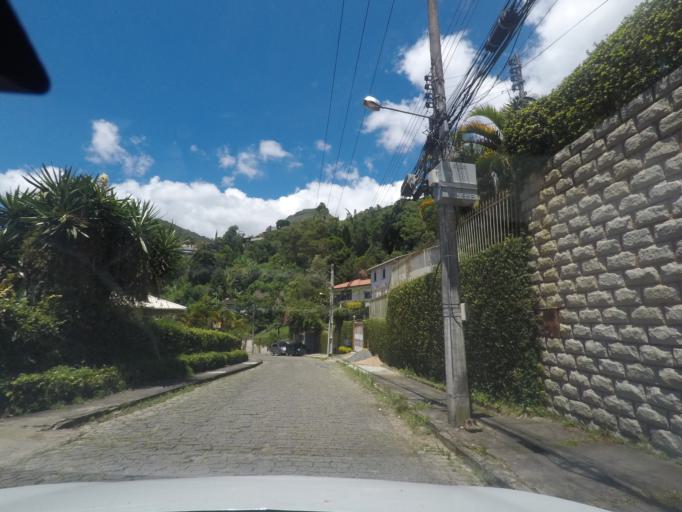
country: BR
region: Rio de Janeiro
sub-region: Teresopolis
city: Teresopolis
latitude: -22.4200
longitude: -42.9826
